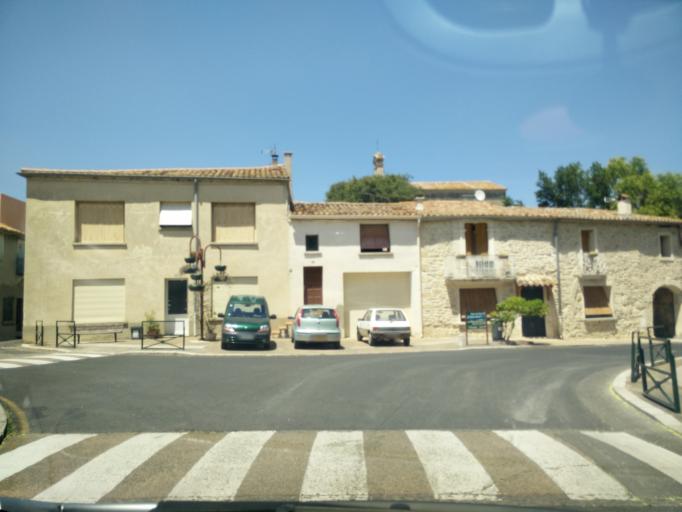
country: FR
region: Languedoc-Roussillon
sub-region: Departement de l'Herault
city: Villetelle
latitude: 43.7215
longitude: 4.1135
